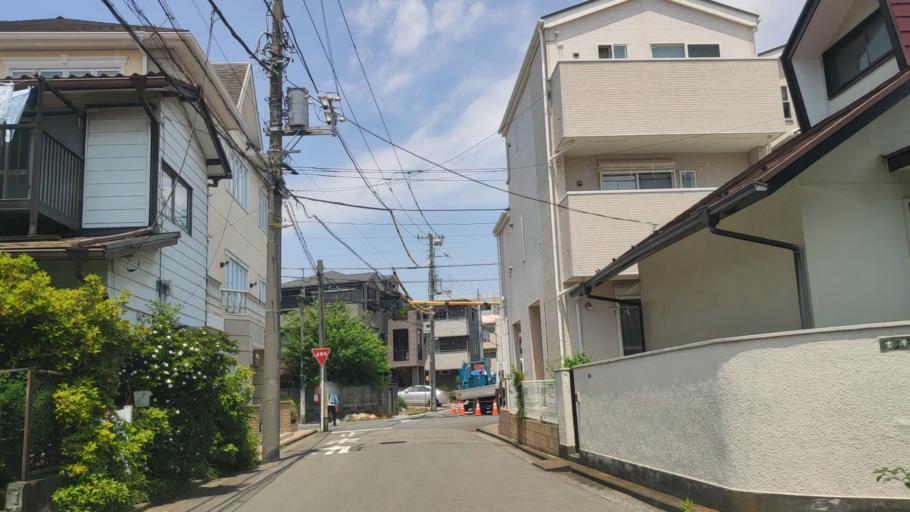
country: JP
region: Kanagawa
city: Yokohama
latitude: 35.4201
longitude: 139.6658
